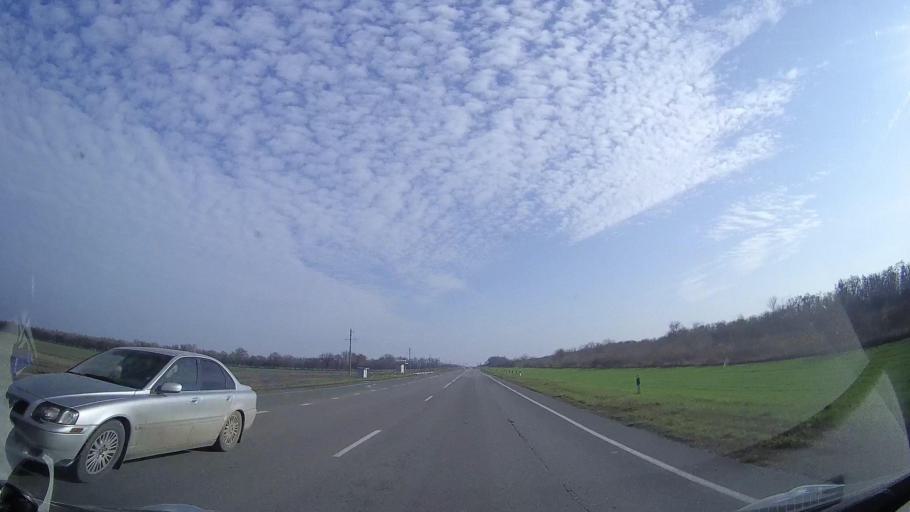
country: RU
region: Rostov
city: Gigant
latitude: 46.5264
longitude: 41.2257
